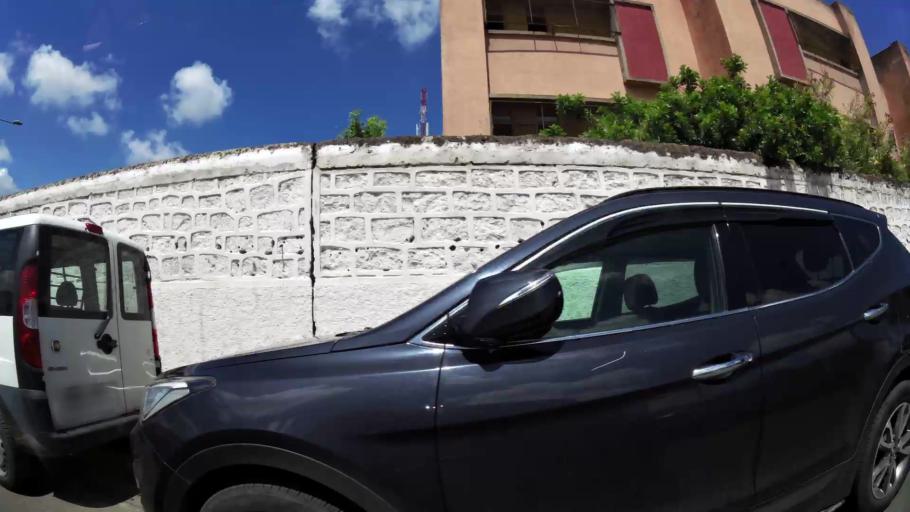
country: MA
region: Grand Casablanca
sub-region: Casablanca
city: Casablanca
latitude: 33.5667
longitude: -7.6043
